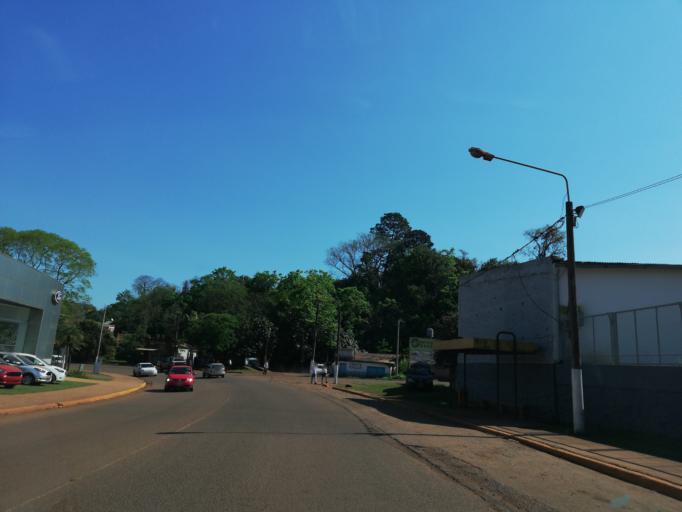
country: AR
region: Misiones
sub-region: Departamento de Eldorado
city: Eldorado
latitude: -26.4071
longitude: -54.6470
